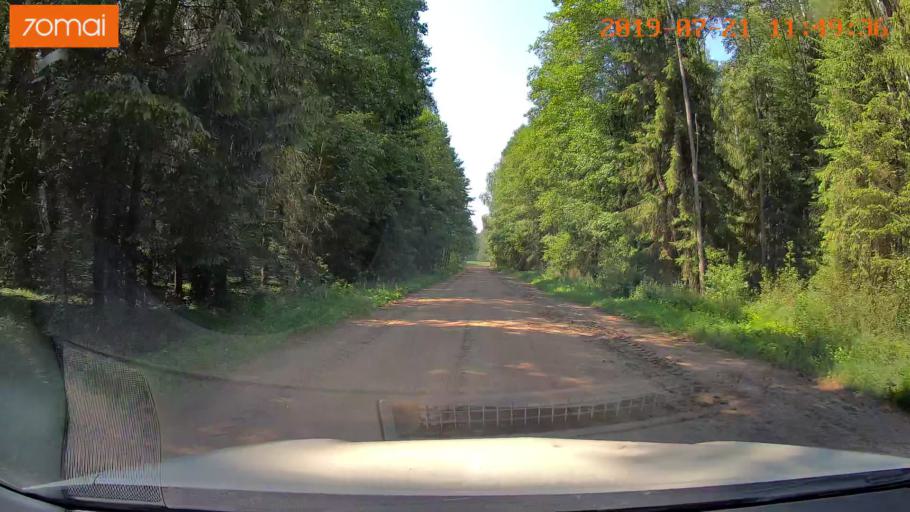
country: BY
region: Grodnenskaya
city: Lyubcha
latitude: 53.8915
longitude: 26.0370
